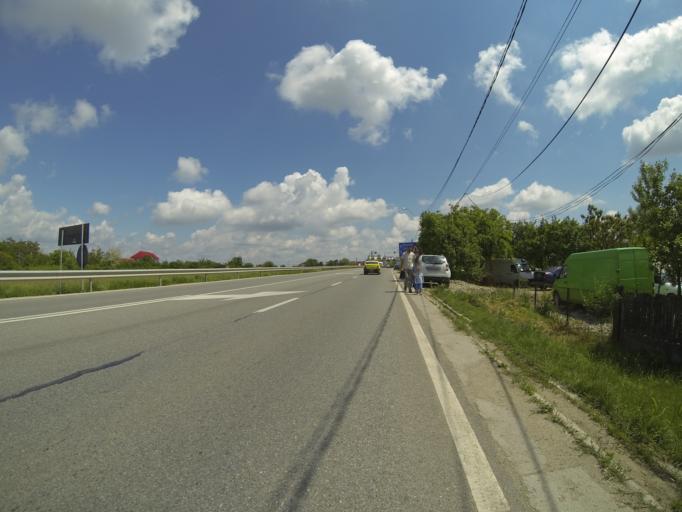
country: RO
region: Dolj
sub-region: Comuna Carcea
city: Carcea
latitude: 44.2647
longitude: 23.8978
